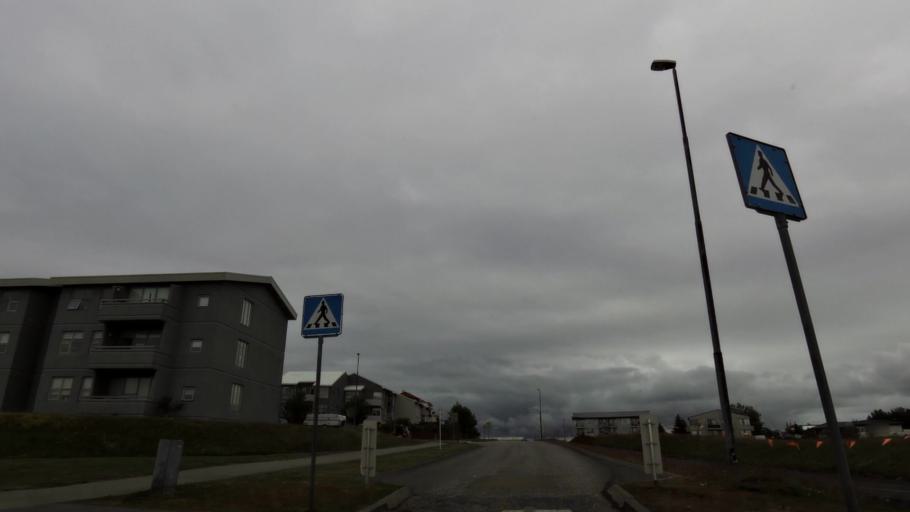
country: IS
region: Capital Region
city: Hafnarfjoerdur
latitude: 64.0549
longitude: -21.9784
